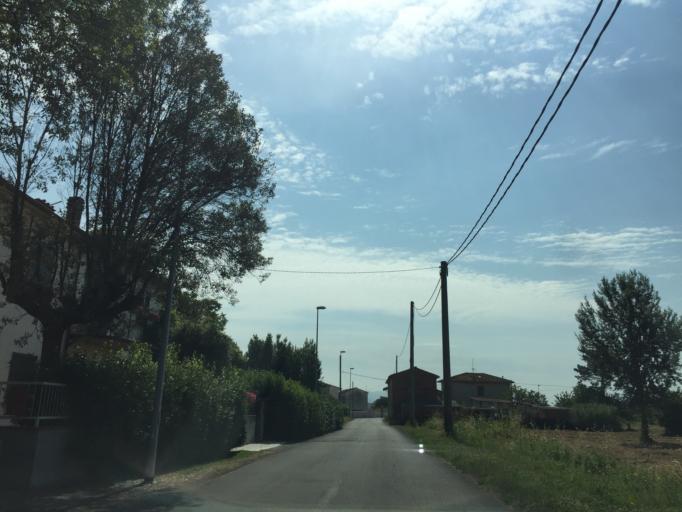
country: IT
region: Tuscany
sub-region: Provincia di Pistoia
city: Ponte Buggianese
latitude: 43.8620
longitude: 10.7542
